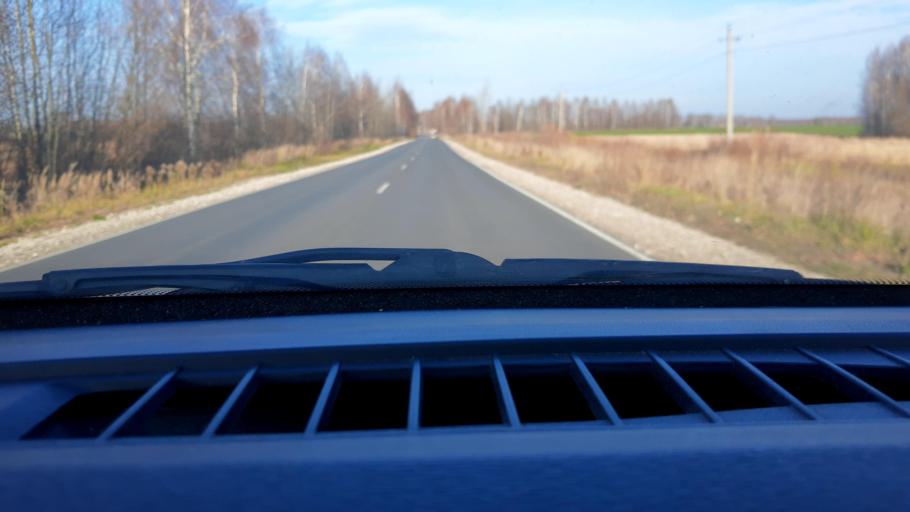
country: RU
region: Nizjnij Novgorod
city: Neklyudovo
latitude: 56.4597
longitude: 43.9034
